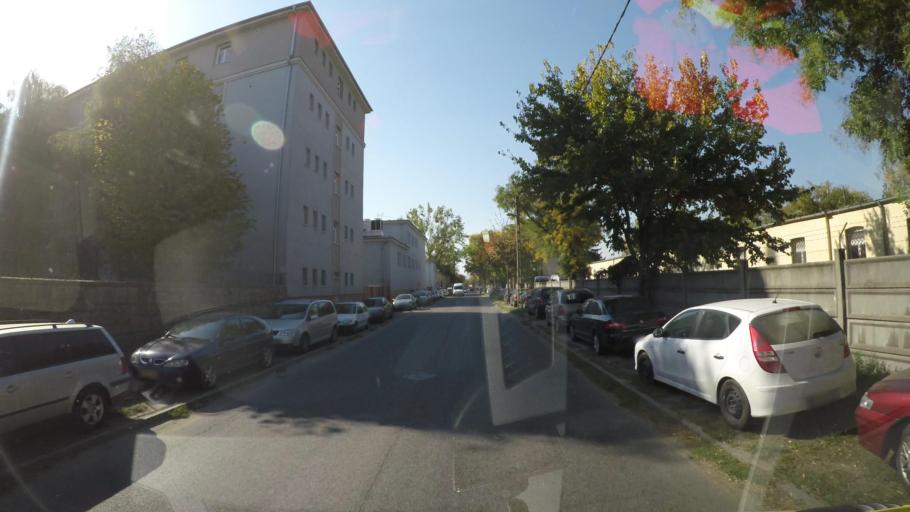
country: HU
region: Budapest
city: Budapest XIV. keruelet
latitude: 47.4969
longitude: 19.1127
